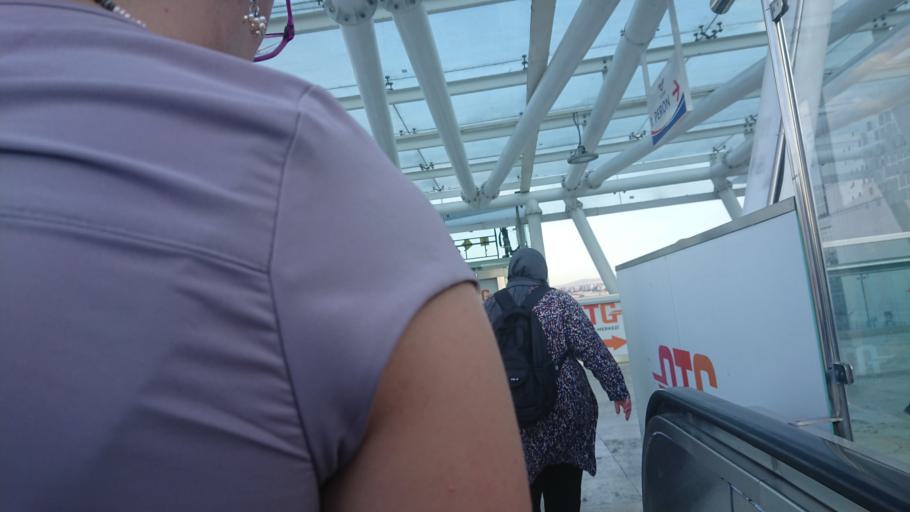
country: TR
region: Ankara
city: Ankara
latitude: 39.9356
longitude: 32.8439
